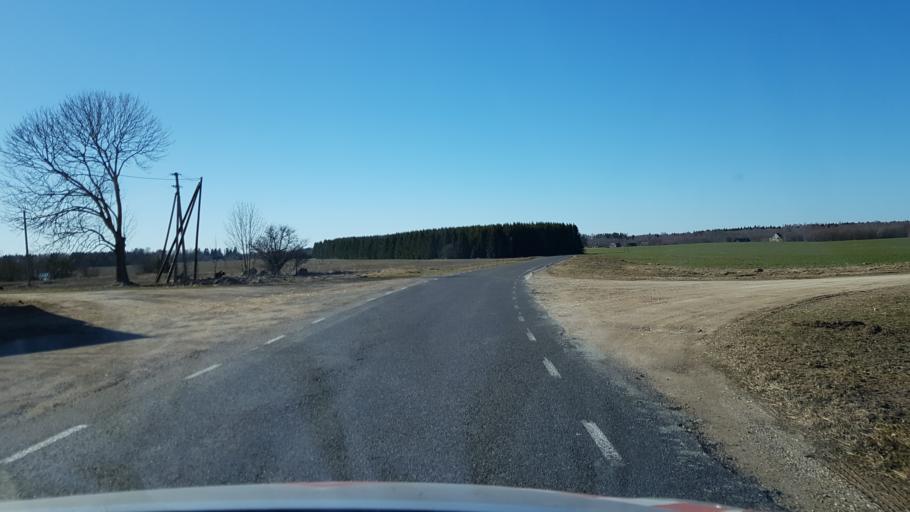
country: EE
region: Laeaene-Virumaa
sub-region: Haljala vald
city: Haljala
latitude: 59.4374
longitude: 26.1750
